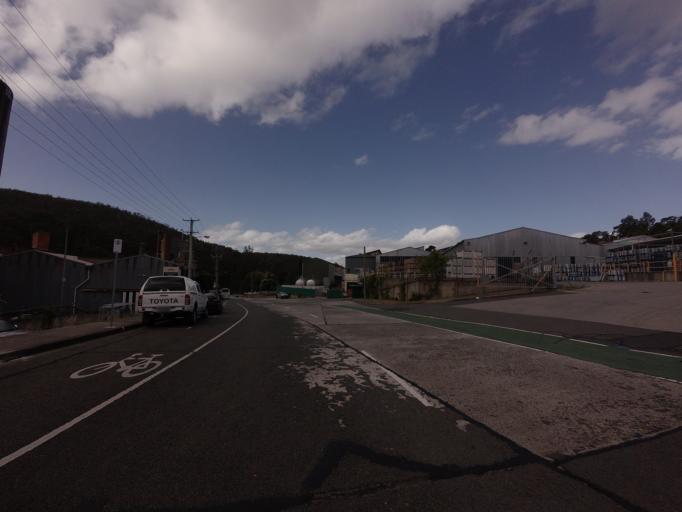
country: AU
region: Tasmania
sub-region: Hobart
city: Dynnyrne
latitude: -42.8970
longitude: 147.2918
